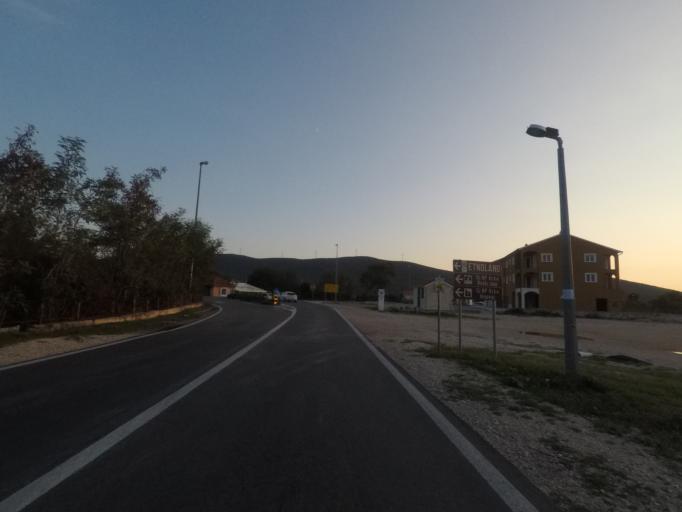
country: HR
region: Sibensko-Kniniska
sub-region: Grad Sibenik
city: Sibenik
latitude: 43.7796
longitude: 15.9649
